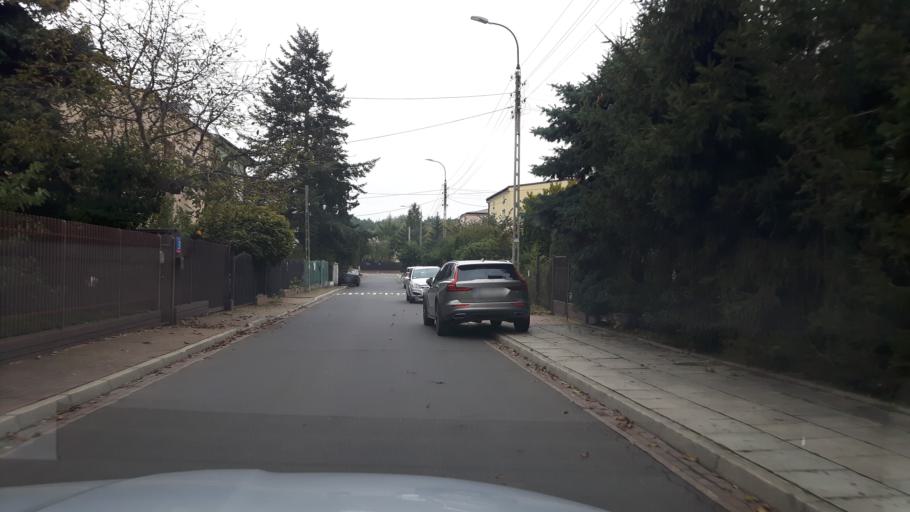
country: PL
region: Masovian Voivodeship
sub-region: Warszawa
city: Praga Poludnie
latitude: 52.2422
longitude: 21.1193
